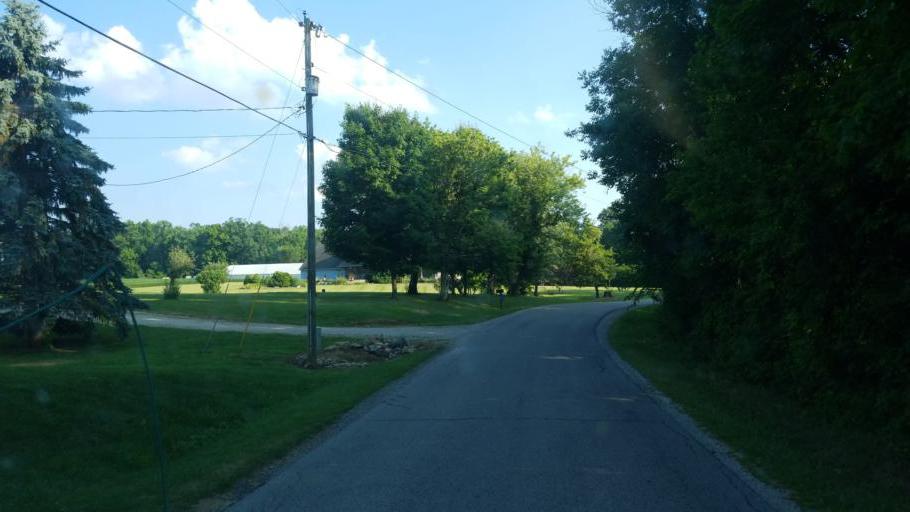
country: US
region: Ohio
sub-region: Crawford County
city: Bucyrus
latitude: 40.8224
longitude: -82.9012
